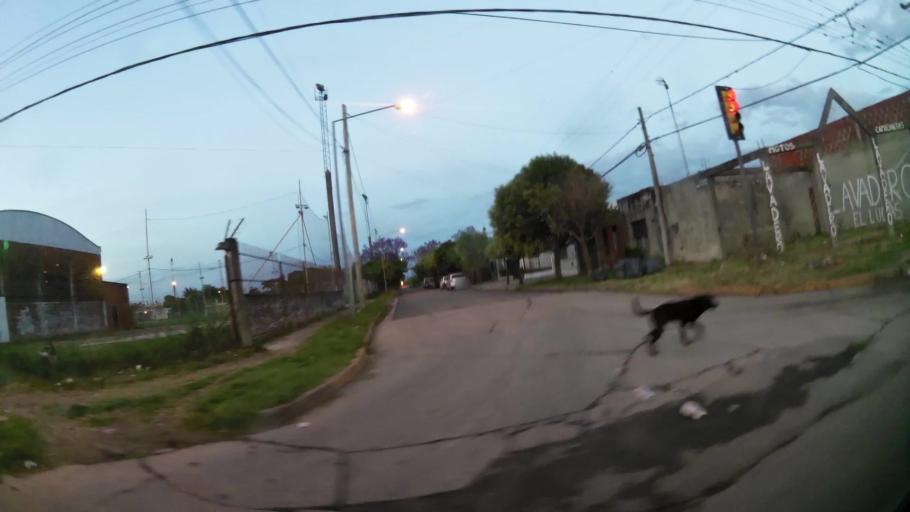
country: AR
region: Buenos Aires
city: San Nicolas de los Arroyos
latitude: -33.3486
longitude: -60.2189
